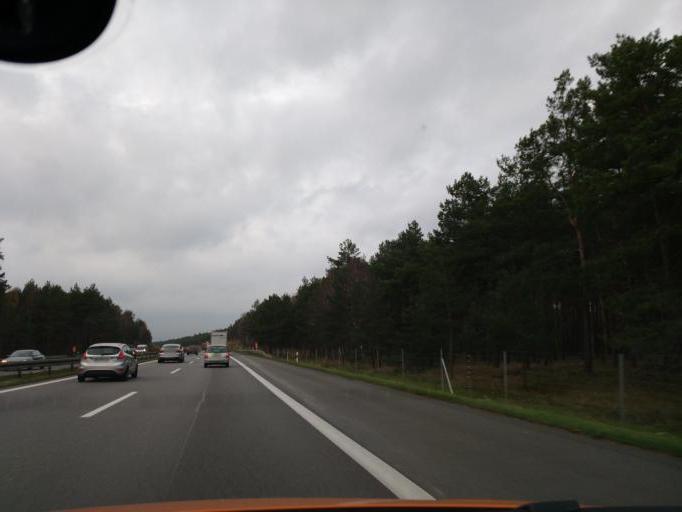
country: DE
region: Brandenburg
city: Wittstock
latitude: 53.0847
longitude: 12.5191
